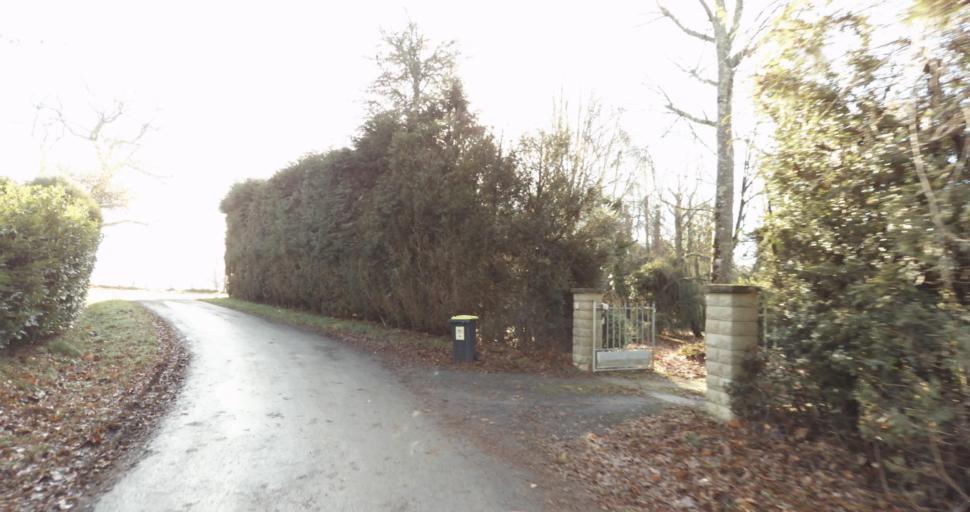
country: FR
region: Limousin
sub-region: Departement de la Haute-Vienne
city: Saint-Priest-sous-Aixe
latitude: 45.7893
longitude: 1.0985
